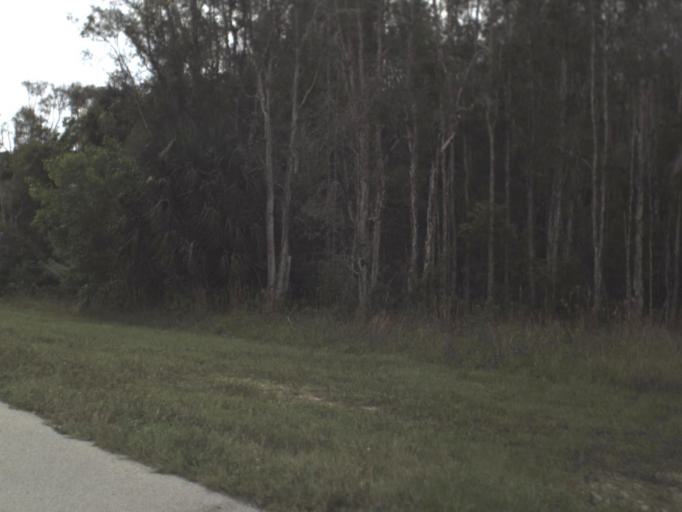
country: US
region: Florida
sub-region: Lee County
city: Pine Manor
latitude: 26.5897
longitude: -81.8530
